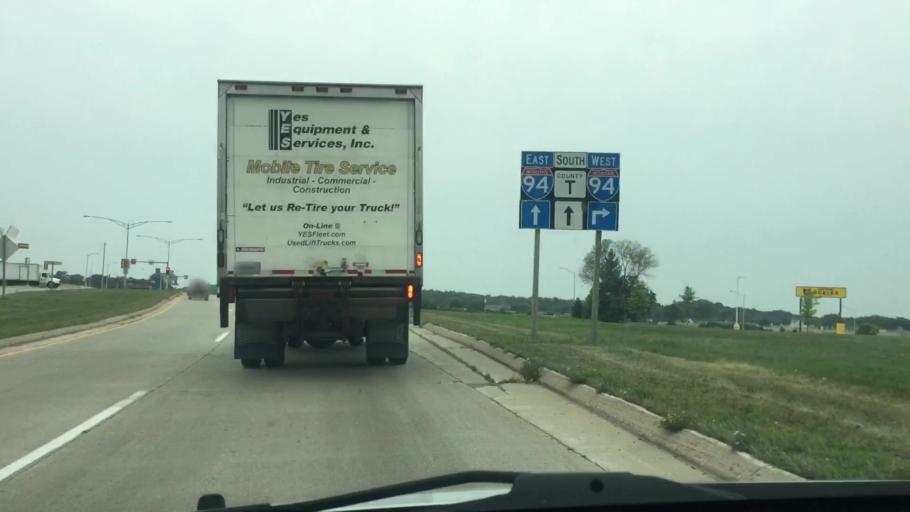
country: US
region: Wisconsin
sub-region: Waukesha County
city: Pewaukee
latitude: 43.0526
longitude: -88.2537
